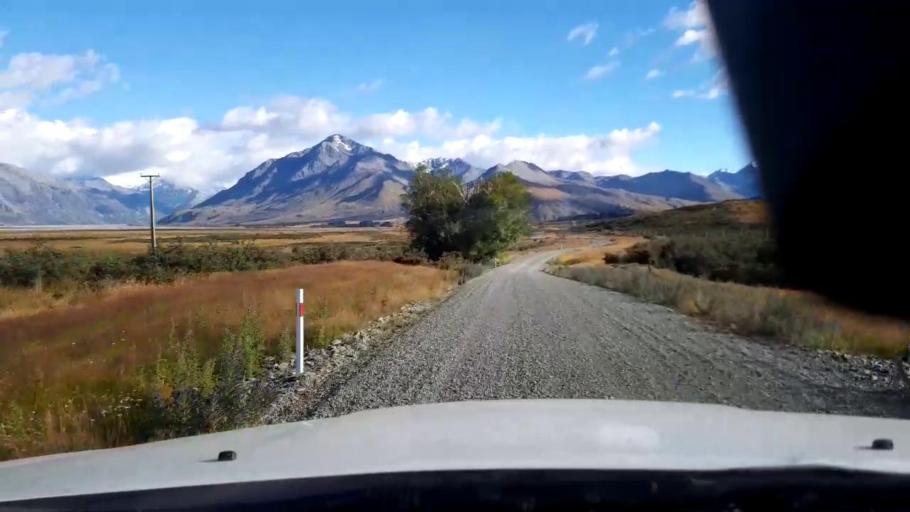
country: NZ
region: Canterbury
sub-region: Timaru District
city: Pleasant Point
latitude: -43.7505
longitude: 170.5711
